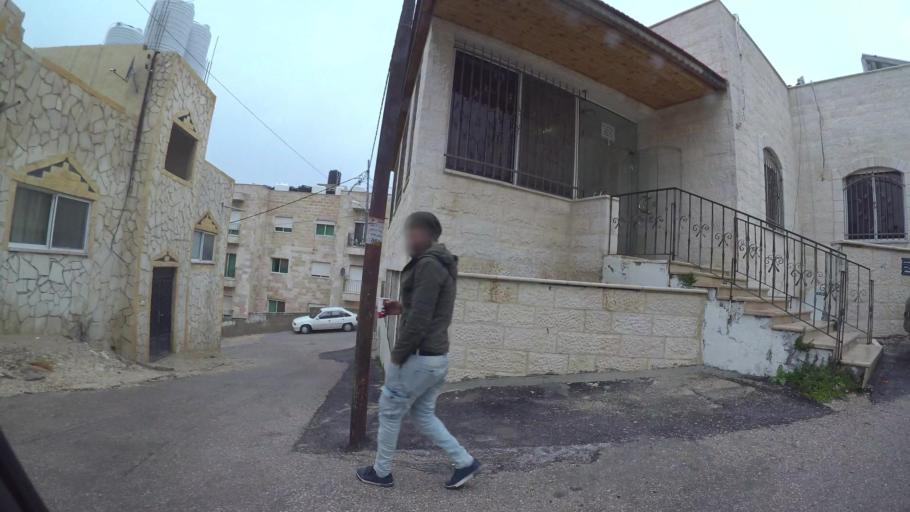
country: JO
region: Amman
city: Al Jubayhah
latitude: 32.0278
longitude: 35.8348
